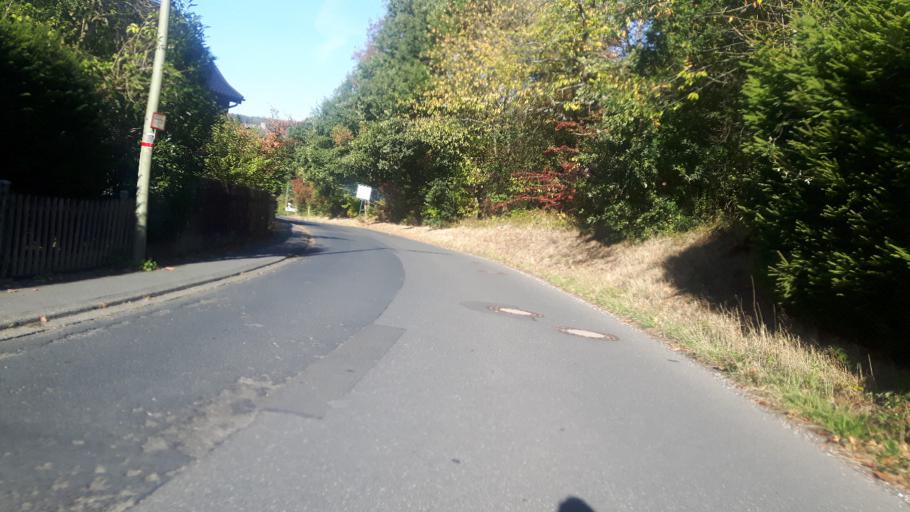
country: DE
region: Rheinland-Pfalz
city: Niederirsen
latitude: 50.8053
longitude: 7.6010
